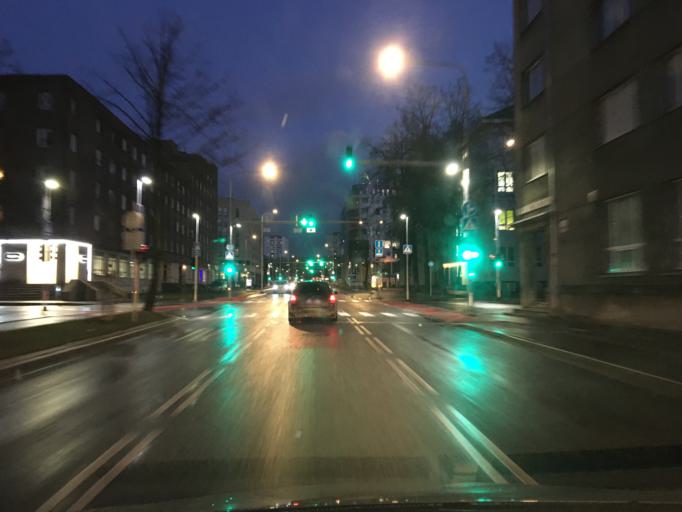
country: EE
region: Harju
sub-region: Tallinna linn
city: Tallinn
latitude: 59.4333
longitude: 24.7758
